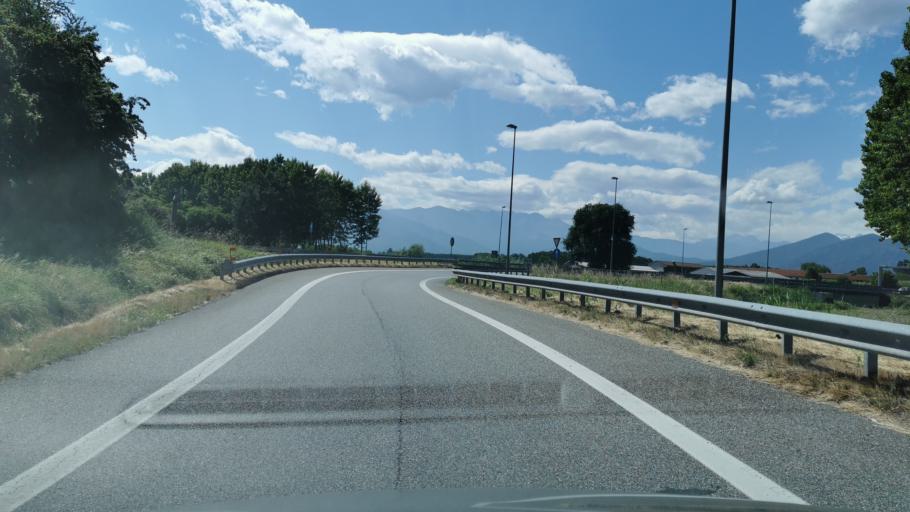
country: IT
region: Piedmont
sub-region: Provincia di Torino
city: Volvera
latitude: 44.9415
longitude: 7.5058
